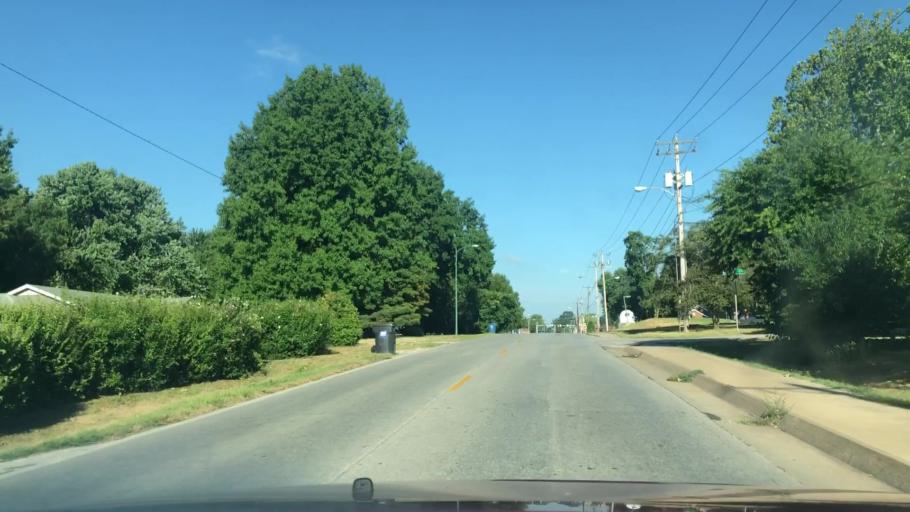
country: US
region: Missouri
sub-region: Greene County
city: Springfield
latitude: 37.1741
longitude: -93.2577
